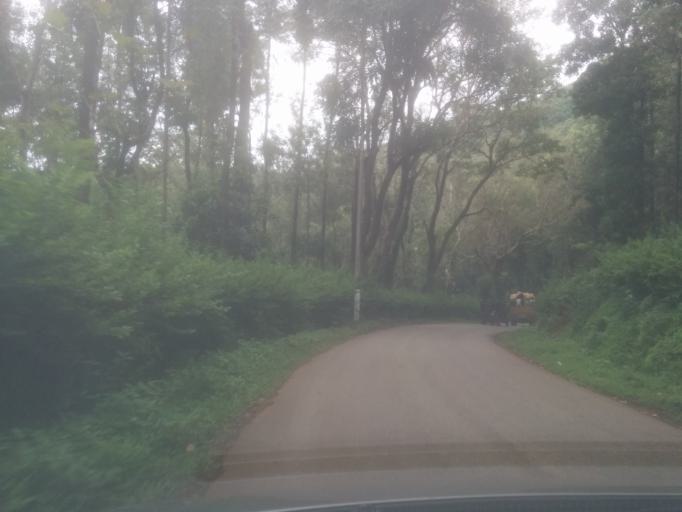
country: IN
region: Karnataka
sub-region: Chikmagalur
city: Chikmagalur
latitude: 13.3799
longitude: 75.7251
